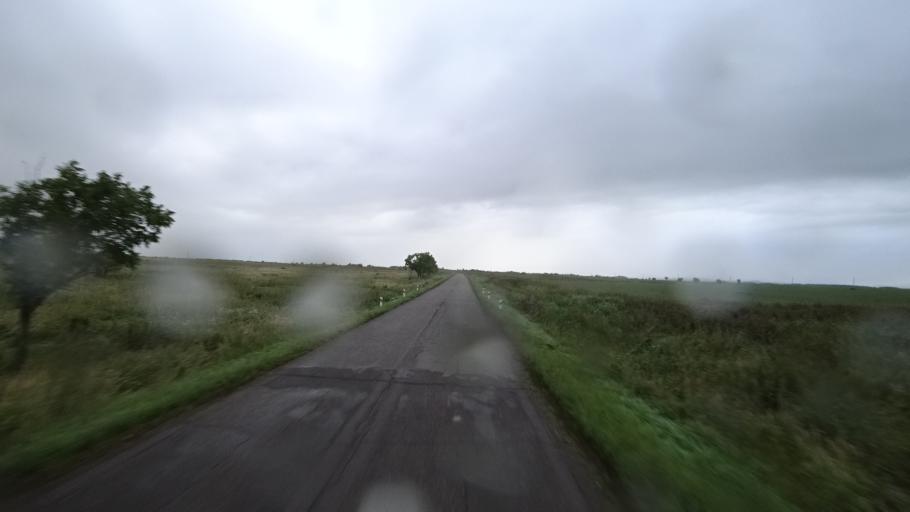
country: RU
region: Primorskiy
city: Chernigovka
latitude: 44.3857
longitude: 132.5295
